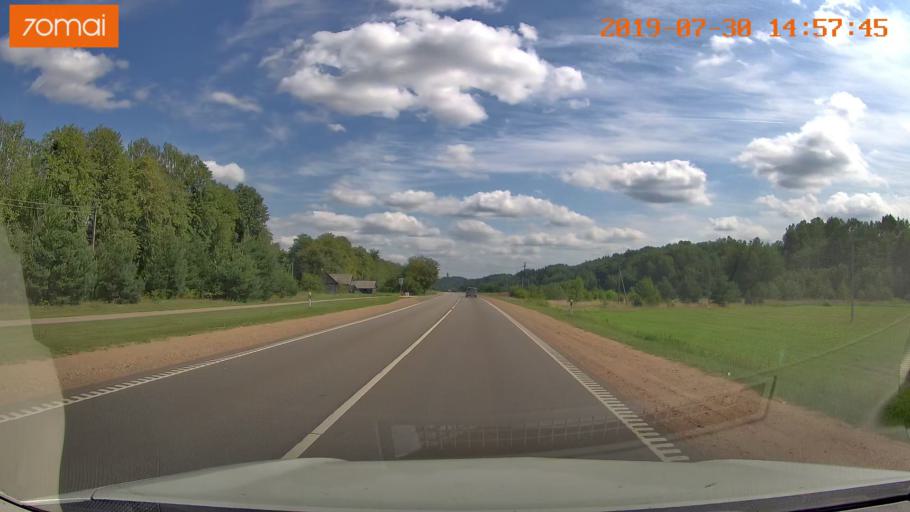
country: LT
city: Prienai
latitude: 54.6165
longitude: 23.9809
